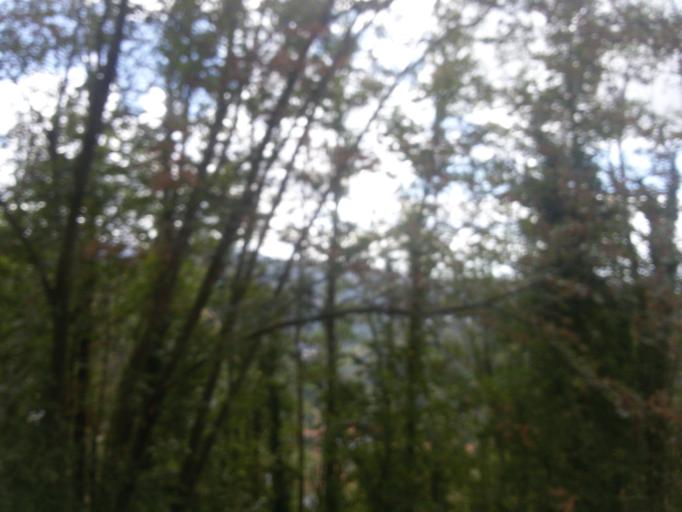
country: IT
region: Liguria
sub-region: Provincia di Genova
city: Piccarello
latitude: 44.4618
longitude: 8.9517
